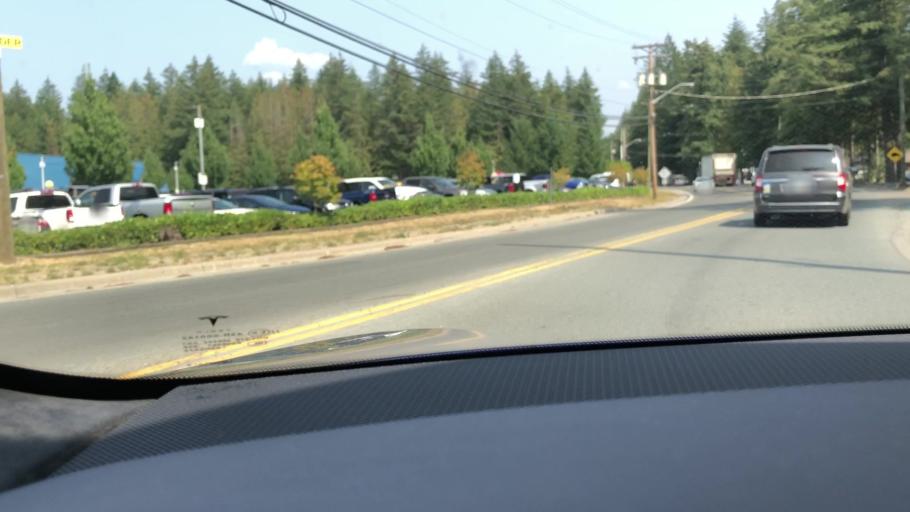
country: CA
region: British Columbia
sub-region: Fraser Valley Regional District
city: Chilliwack
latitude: 49.0751
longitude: -121.9760
